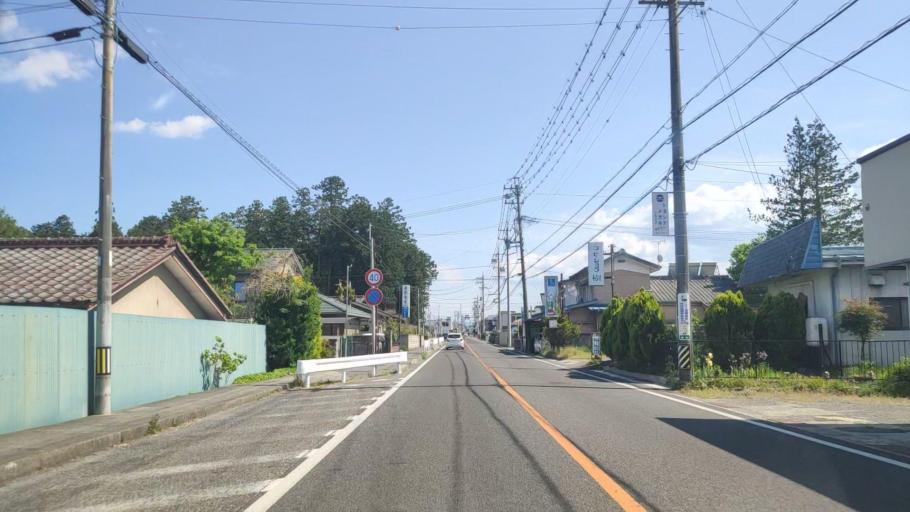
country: JP
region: Nagano
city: Toyoshina
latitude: 36.2932
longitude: 137.9063
